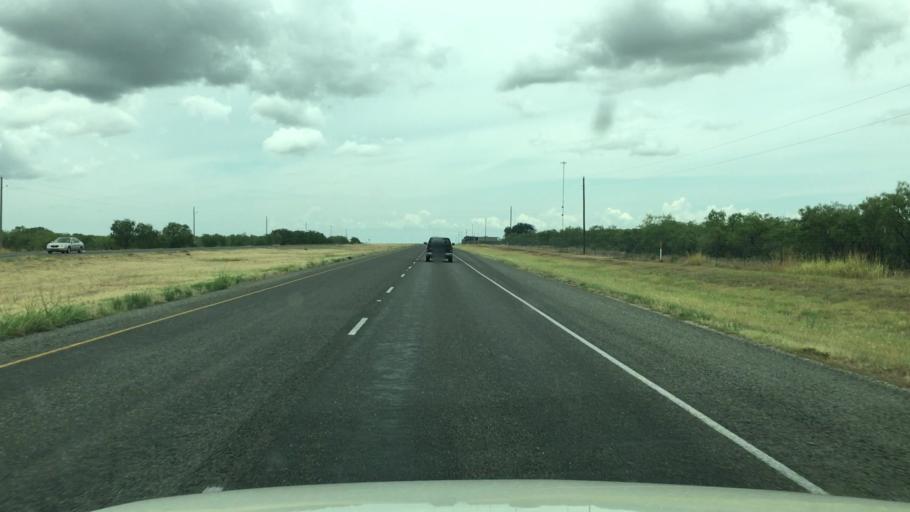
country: US
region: Texas
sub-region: Concho County
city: Eden
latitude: 31.2222
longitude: -99.9715
